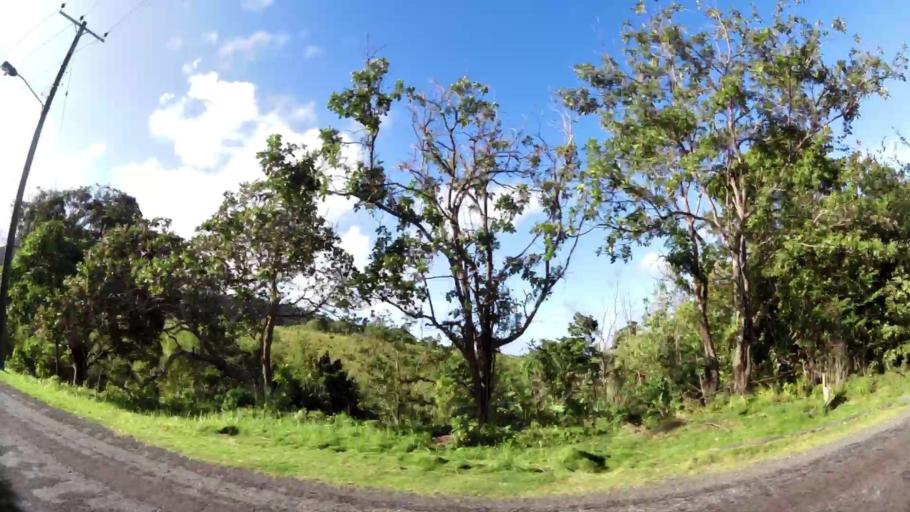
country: LC
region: Anse-la-Raye
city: Anse La Raye
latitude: 13.9221
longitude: -61.0421
